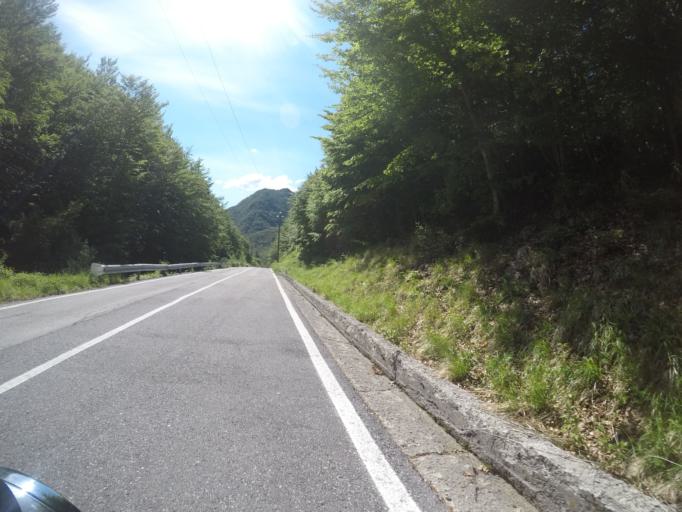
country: IT
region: Tuscany
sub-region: Provincia di Lucca
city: Seravezza
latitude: 44.0617
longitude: 10.2351
